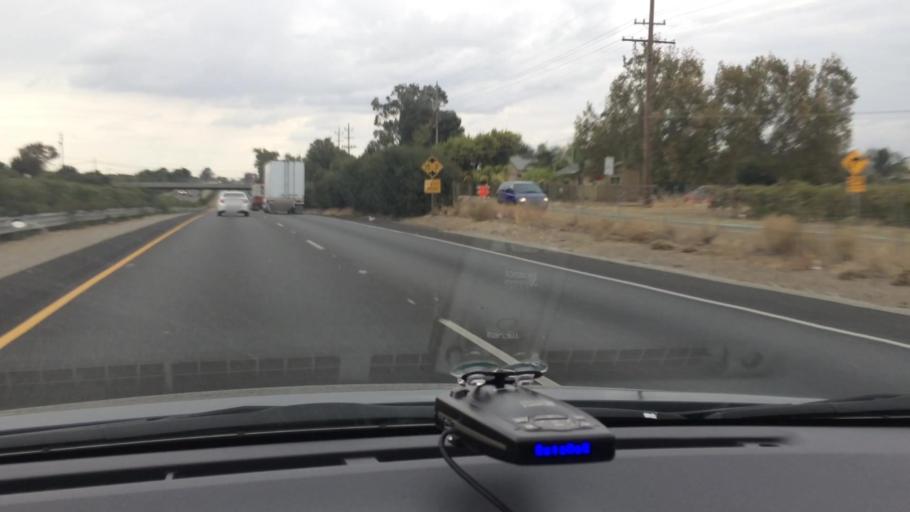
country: US
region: California
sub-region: San Joaquin County
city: Collierville
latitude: 38.1723
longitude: -121.2621
